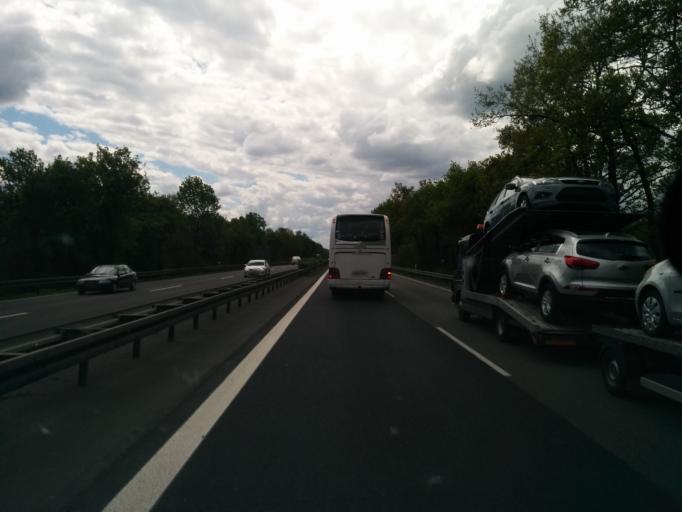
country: DE
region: Brandenburg
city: Werder
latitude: 52.4568
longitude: 12.9374
